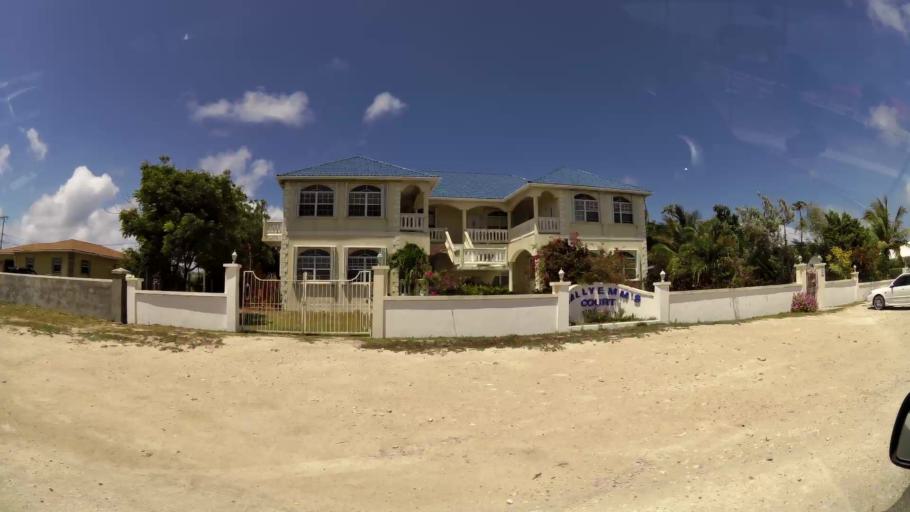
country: TC
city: Cockburn Town
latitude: 21.4503
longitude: -71.1468
